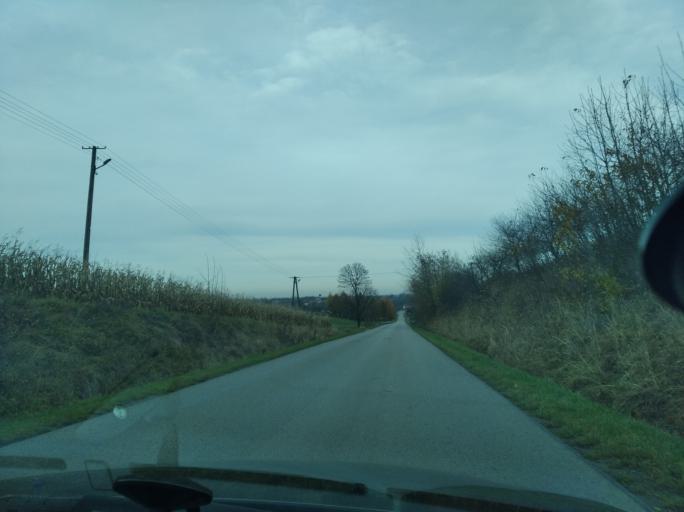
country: PL
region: Subcarpathian Voivodeship
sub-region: Powiat przeworski
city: Debow
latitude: 50.0401
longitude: 22.4286
